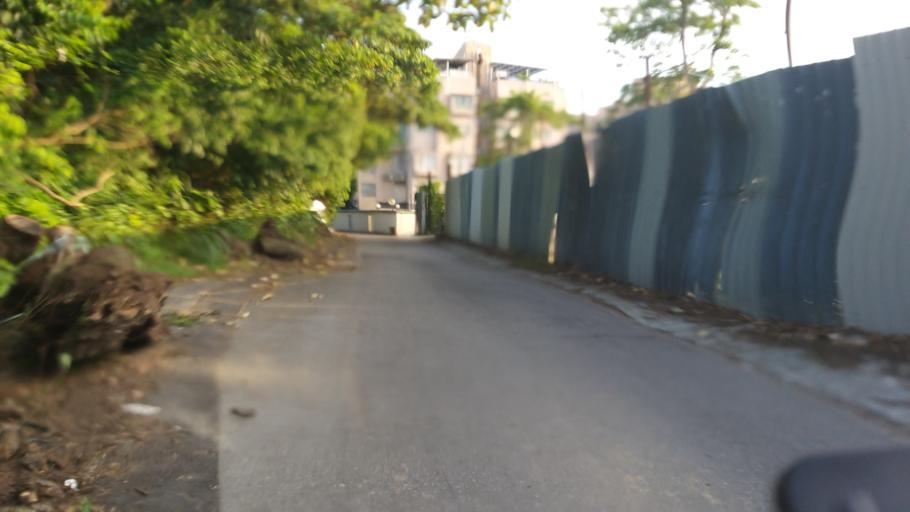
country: HK
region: Yuen Long
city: Yuen Long Kau Hui
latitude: 22.4446
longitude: 114.0135
